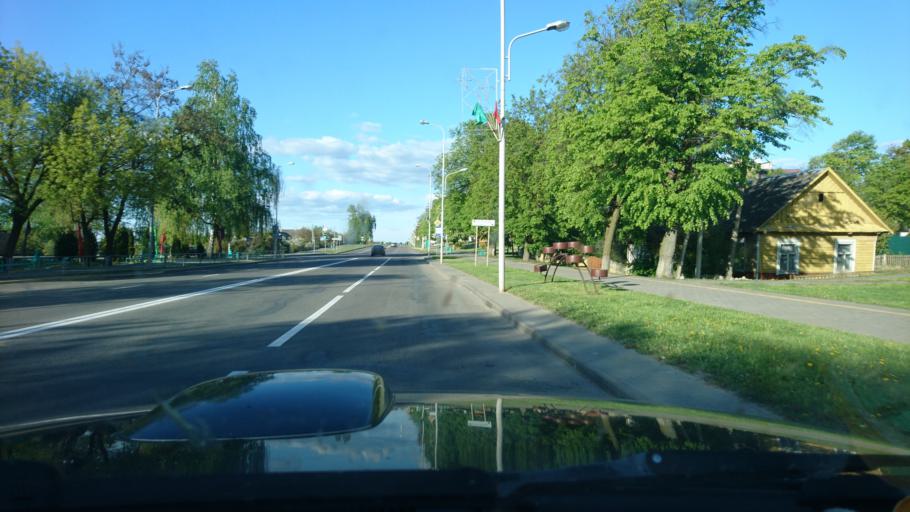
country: BY
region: Brest
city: Ivatsevichy
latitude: 52.7138
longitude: 25.3472
